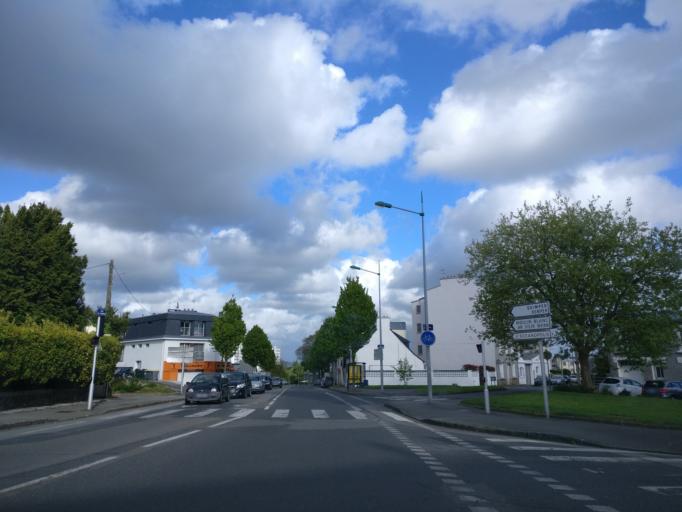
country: FR
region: Brittany
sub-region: Departement du Finistere
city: Brest
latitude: 48.4014
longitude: -4.4561
